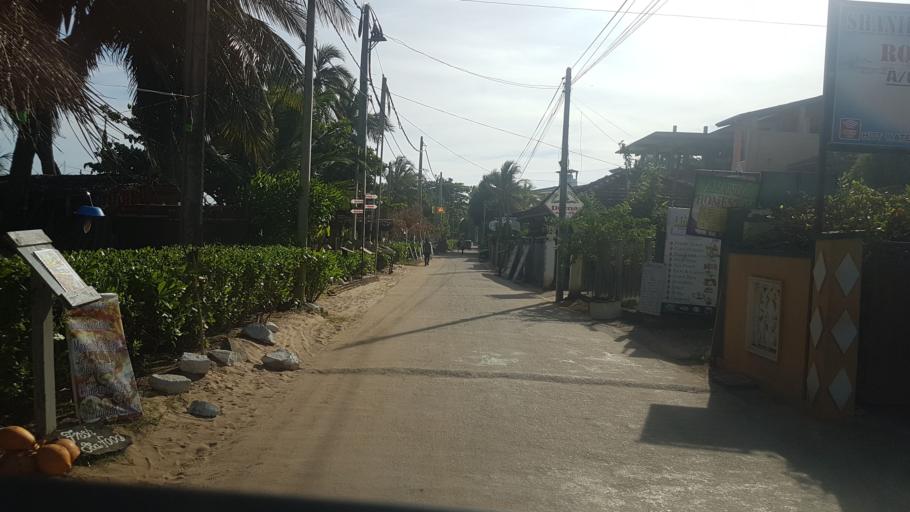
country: LK
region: Southern
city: Tangalla
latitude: 6.0339
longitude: 80.8015
